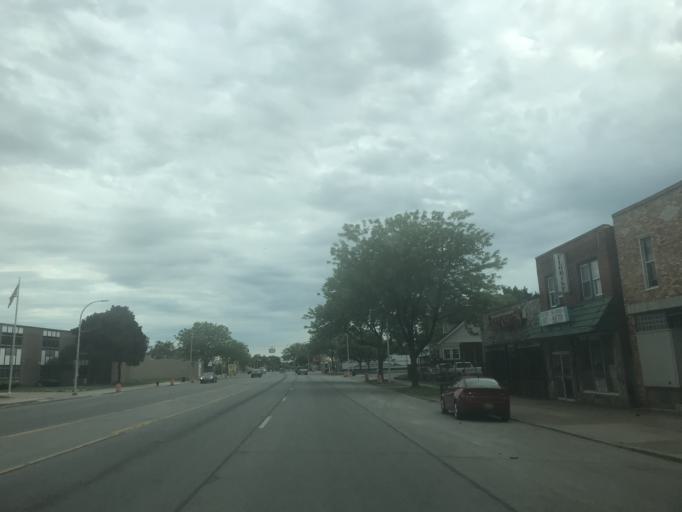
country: US
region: Michigan
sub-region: Wayne County
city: River Rouge
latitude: 42.2653
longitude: -83.1367
